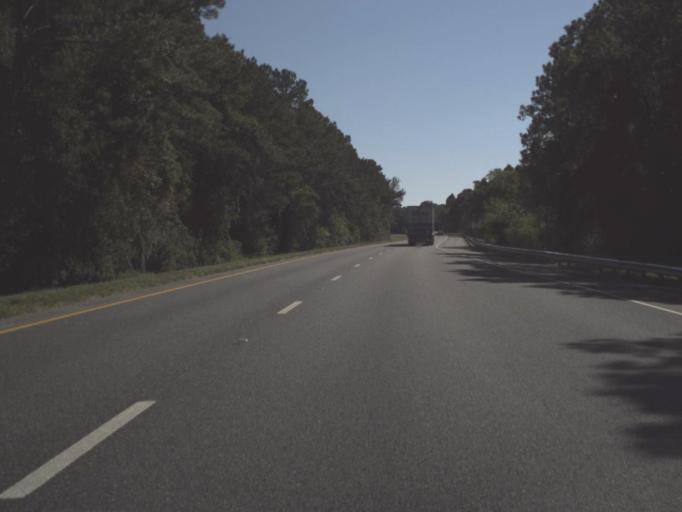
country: US
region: Florida
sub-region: Sumter County
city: Wildwood
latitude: 28.8339
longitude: -82.0402
